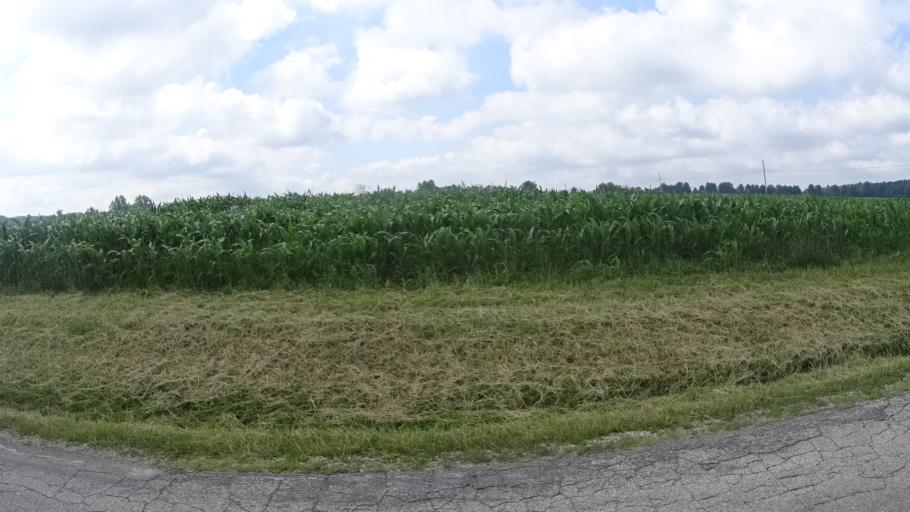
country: US
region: Ohio
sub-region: Huron County
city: Wakeman
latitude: 41.3058
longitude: -82.4124
